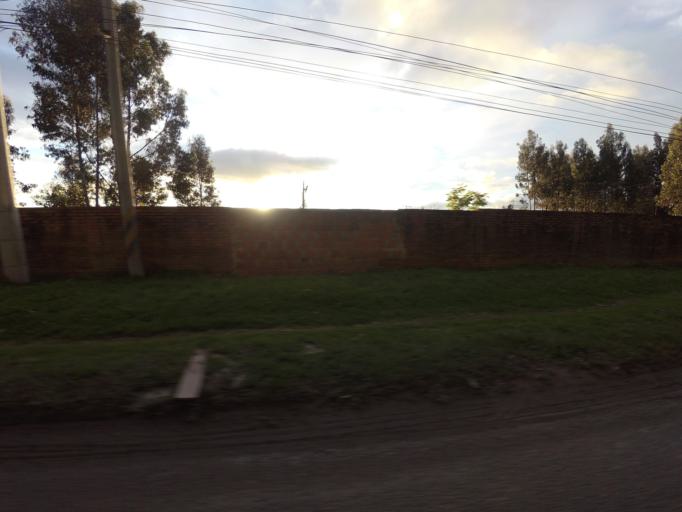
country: CO
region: Cundinamarca
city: La Calera
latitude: 4.7730
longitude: -74.0267
